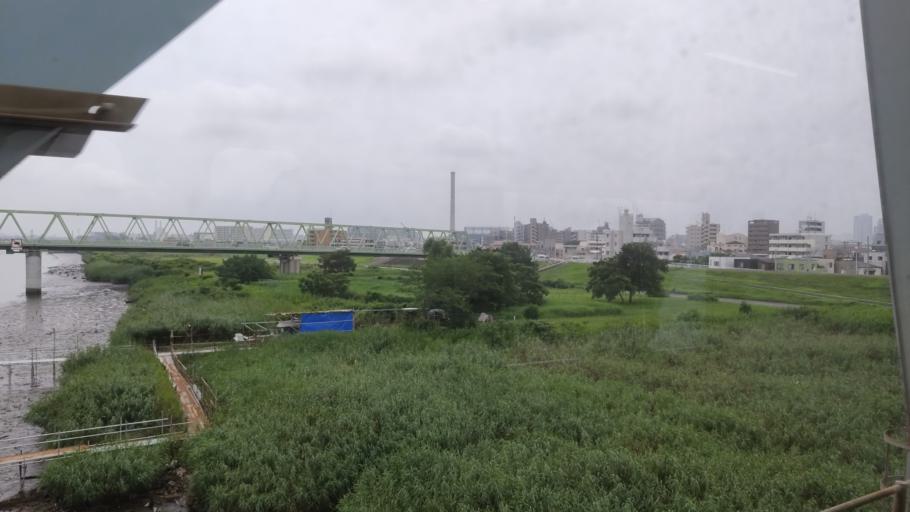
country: JP
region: Tokyo
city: Urayasu
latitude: 35.7288
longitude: 139.8308
